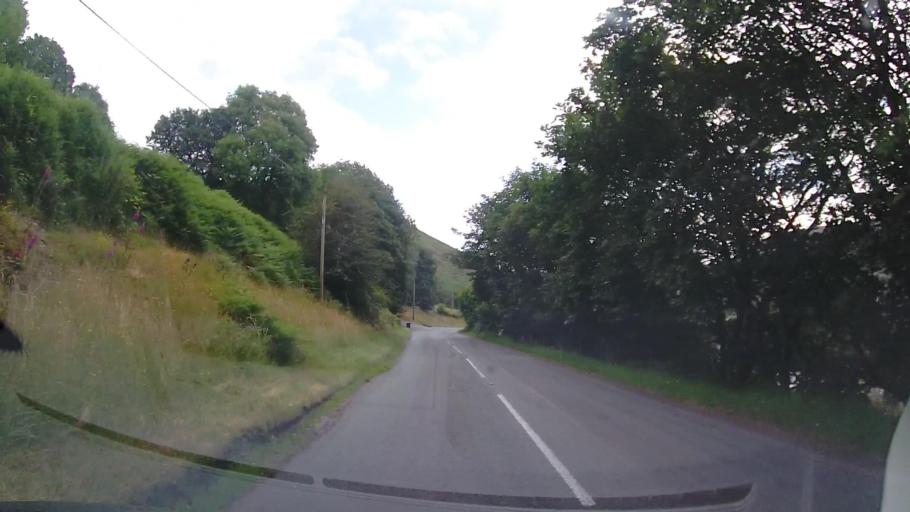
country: GB
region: Wales
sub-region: Sir Powys
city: Llangynog
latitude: 52.8387
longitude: -3.4208
